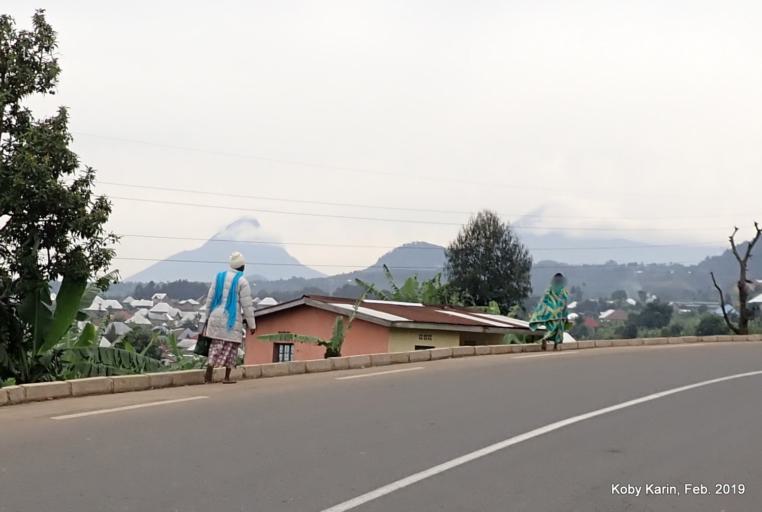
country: RW
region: Western Province
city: Gisenyi
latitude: -1.6918
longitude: 29.3484
